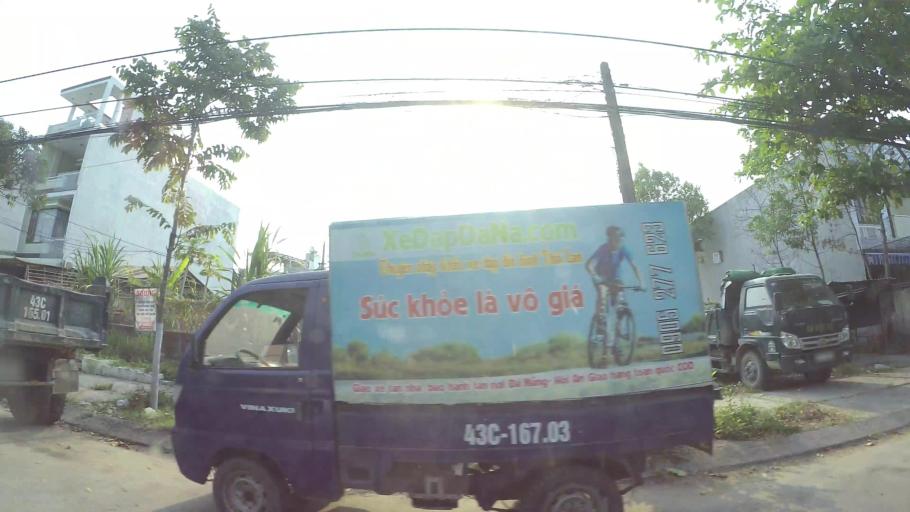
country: VN
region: Da Nang
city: Cam Le
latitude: 16.0195
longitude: 108.2070
